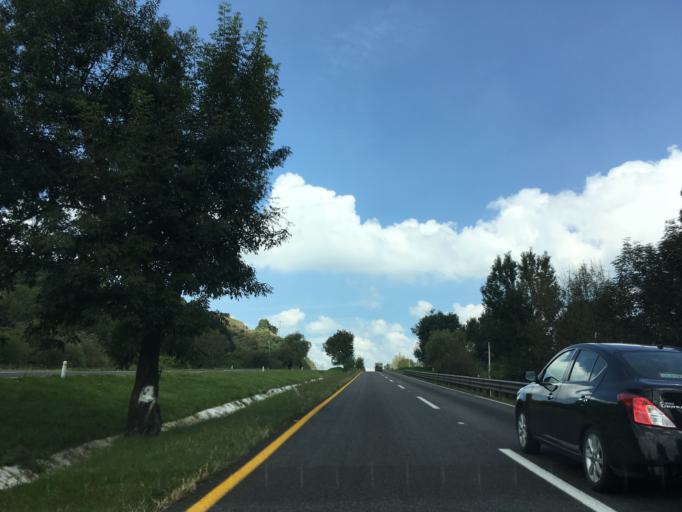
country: MX
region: Michoacan
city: Lagunillas
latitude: 19.5583
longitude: -101.3977
